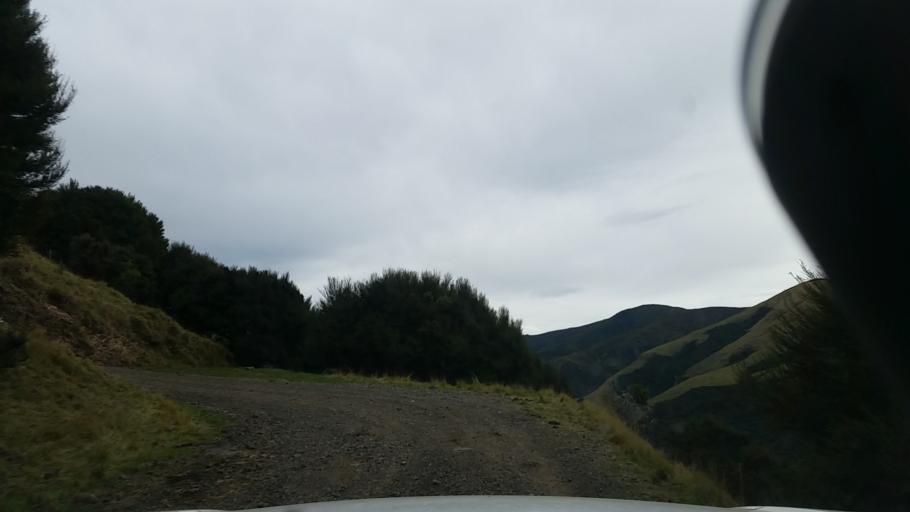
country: NZ
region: Canterbury
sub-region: Christchurch City
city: Christchurch
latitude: -43.8594
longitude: 173.0404
